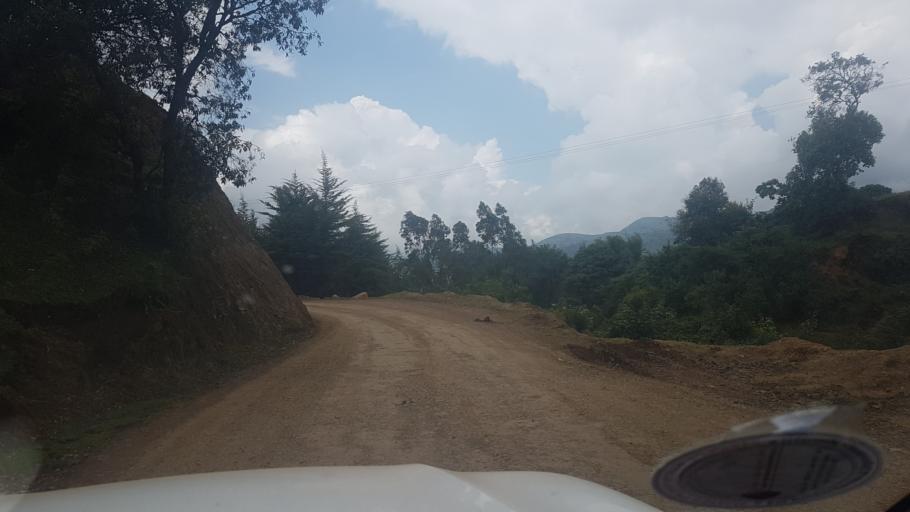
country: ET
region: Southern Nations, Nationalities, and People's Region
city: Arba Minch'
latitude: 6.3225
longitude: 37.5391
